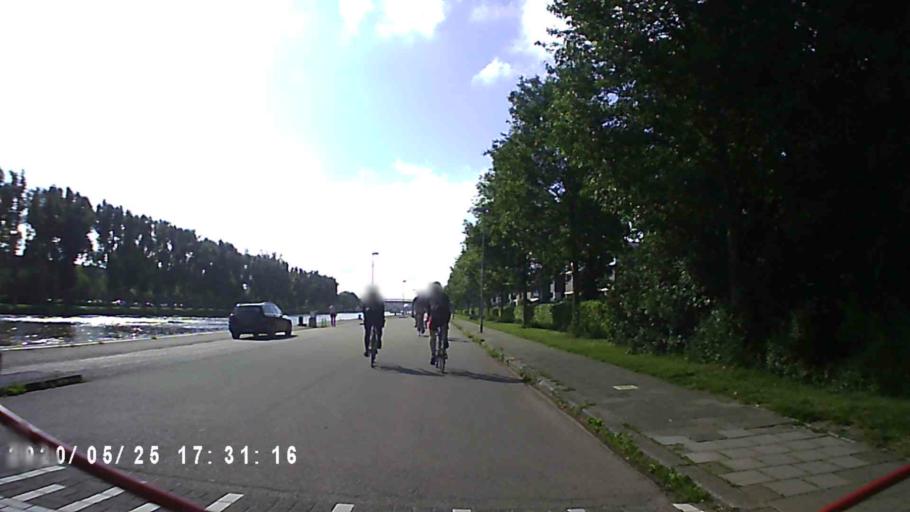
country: NL
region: Groningen
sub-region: Gemeente Groningen
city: Korrewegwijk
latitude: 53.2372
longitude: 6.5763
